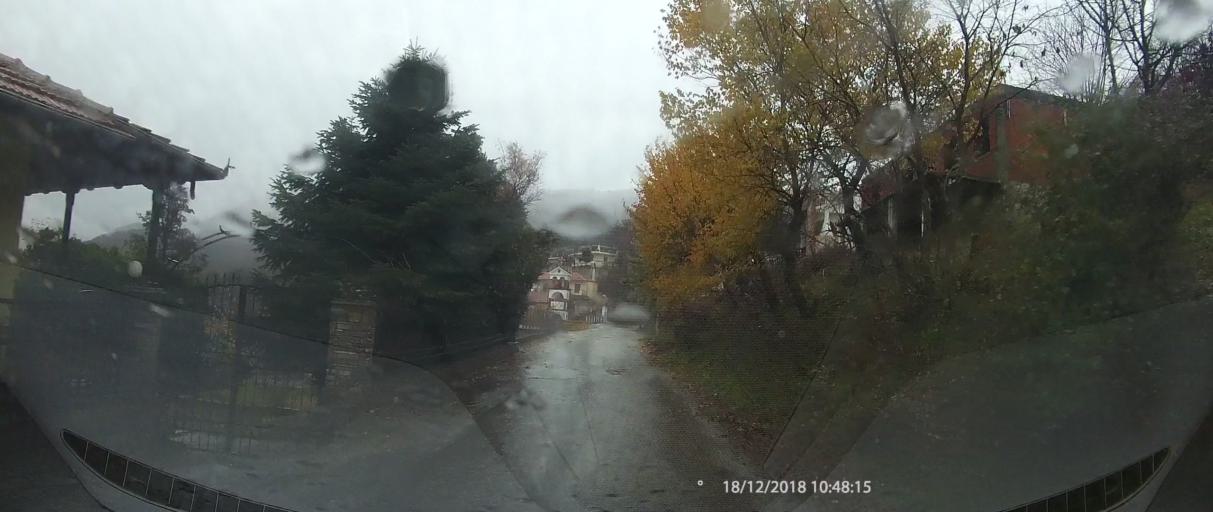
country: GR
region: Central Macedonia
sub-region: Nomos Pierias
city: Kato Milia
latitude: 40.1814
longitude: 22.3304
